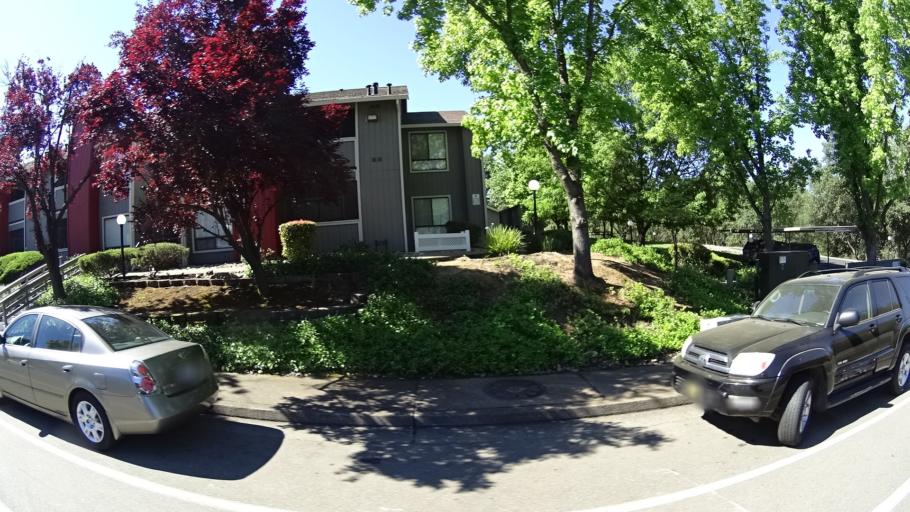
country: US
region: California
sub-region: Placer County
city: Rocklin
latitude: 38.7747
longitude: -121.2533
